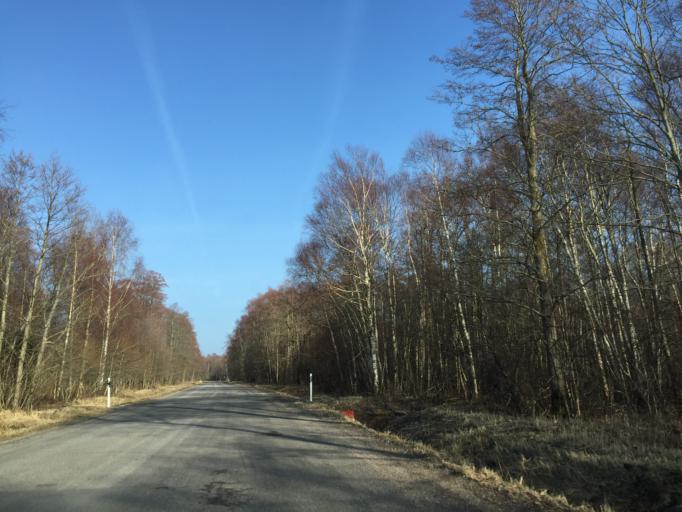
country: EE
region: Saare
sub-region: Kuressaare linn
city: Kuressaare
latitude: 58.0617
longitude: 22.1601
